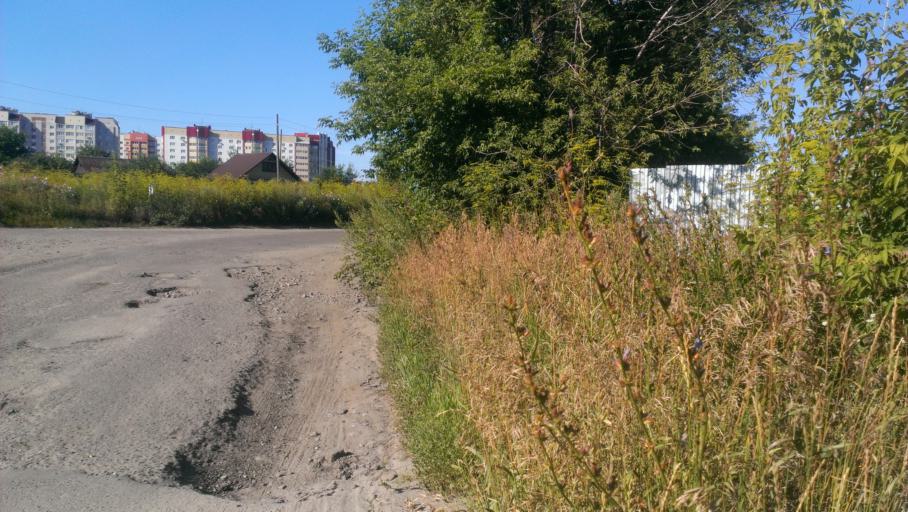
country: RU
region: Altai Krai
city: Novosilikatnyy
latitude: 53.3217
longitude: 83.6805
